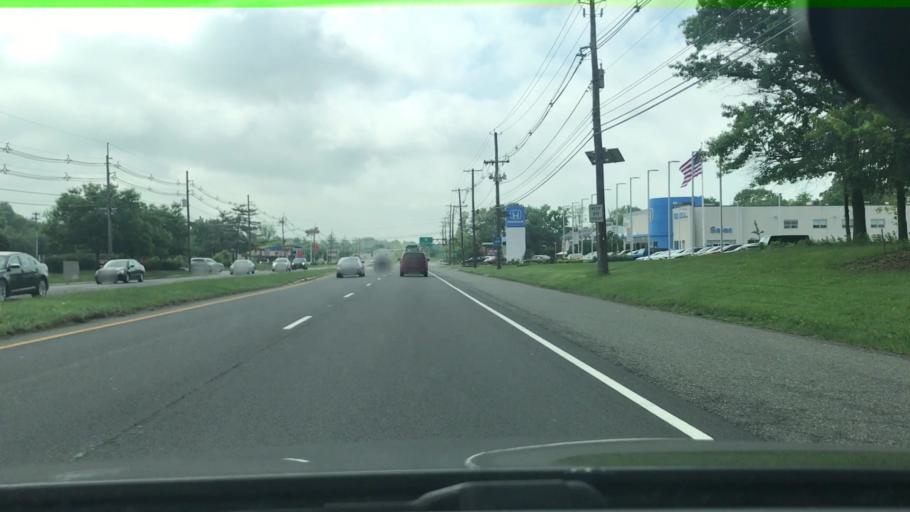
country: US
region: New Jersey
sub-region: Burlington County
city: Marlton
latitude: 39.8994
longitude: -74.9324
